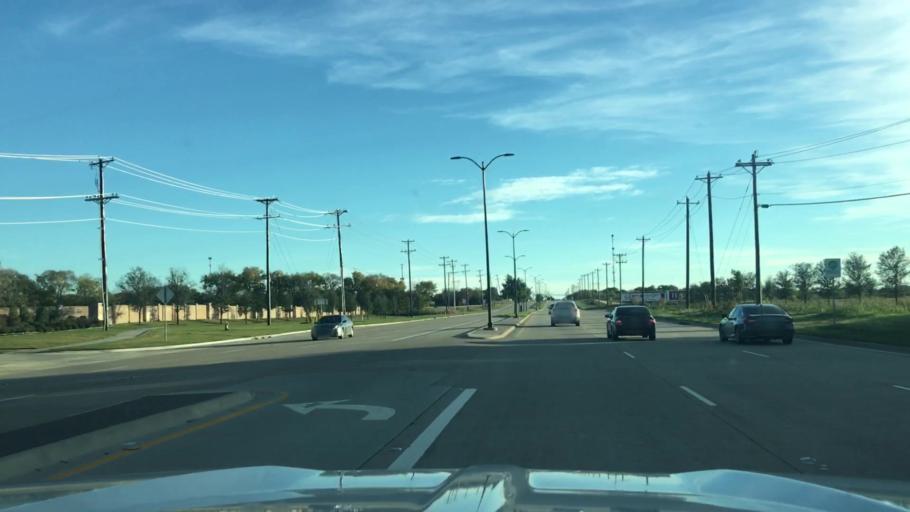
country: US
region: Texas
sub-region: Collin County
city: Prosper
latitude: 33.2135
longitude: -96.8027
